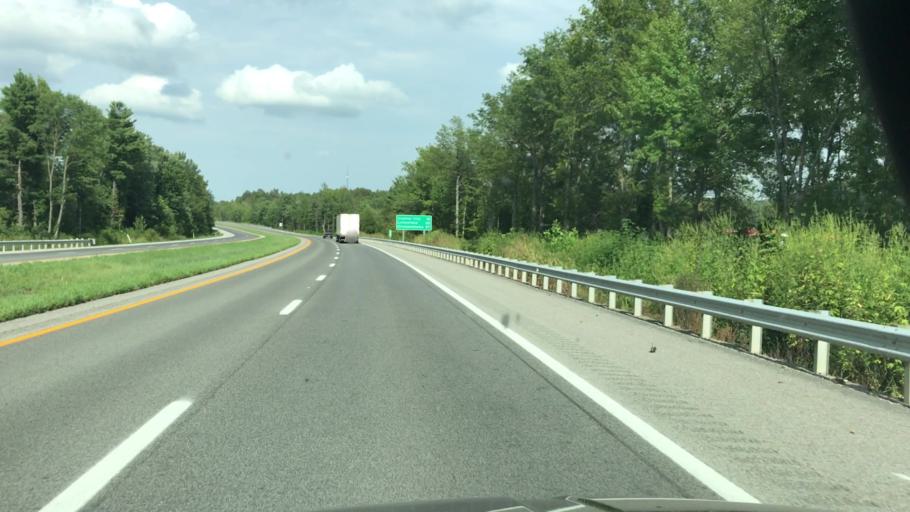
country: US
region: Kentucky
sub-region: Muhlenberg County
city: Greenville
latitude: 37.2374
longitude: -87.2602
